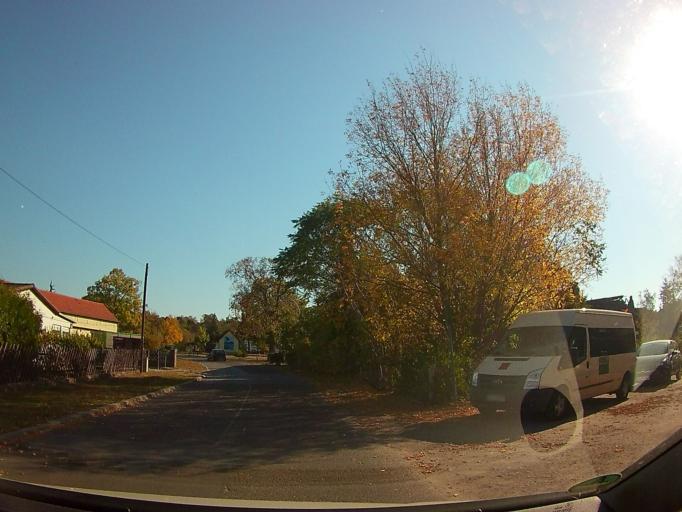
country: DE
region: Brandenburg
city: Baruth
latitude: 52.1154
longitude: 13.5225
